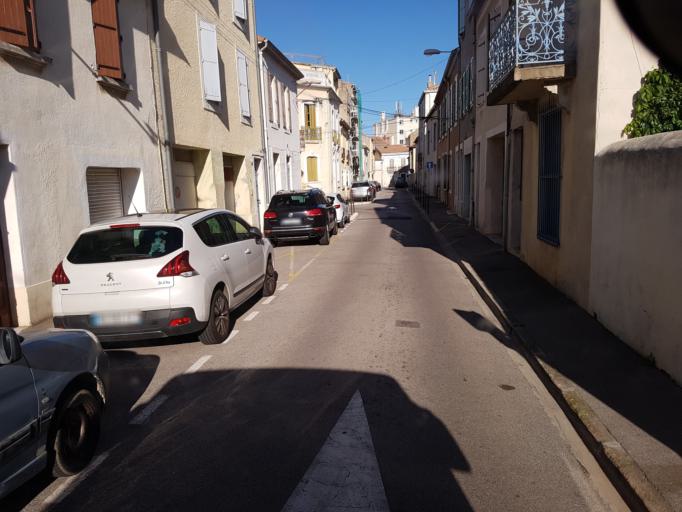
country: FR
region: Languedoc-Roussillon
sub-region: Departement de l'Aude
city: Narbonne
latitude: 43.1798
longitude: 3.0054
